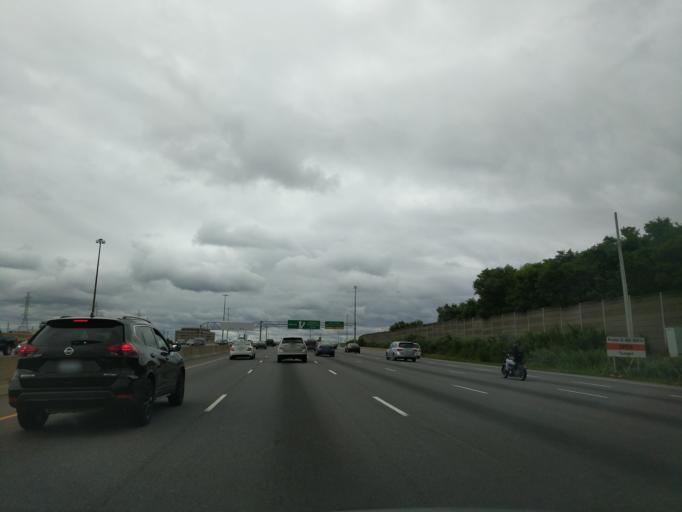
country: CA
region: Ontario
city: Etobicoke
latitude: 43.6877
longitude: -79.5722
